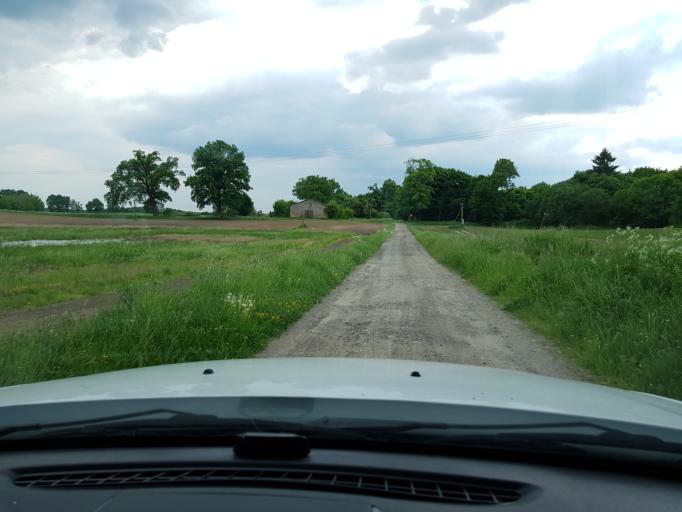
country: PL
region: West Pomeranian Voivodeship
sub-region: Powiat drawski
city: Drawsko Pomorskie
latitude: 53.5378
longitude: 15.7336
